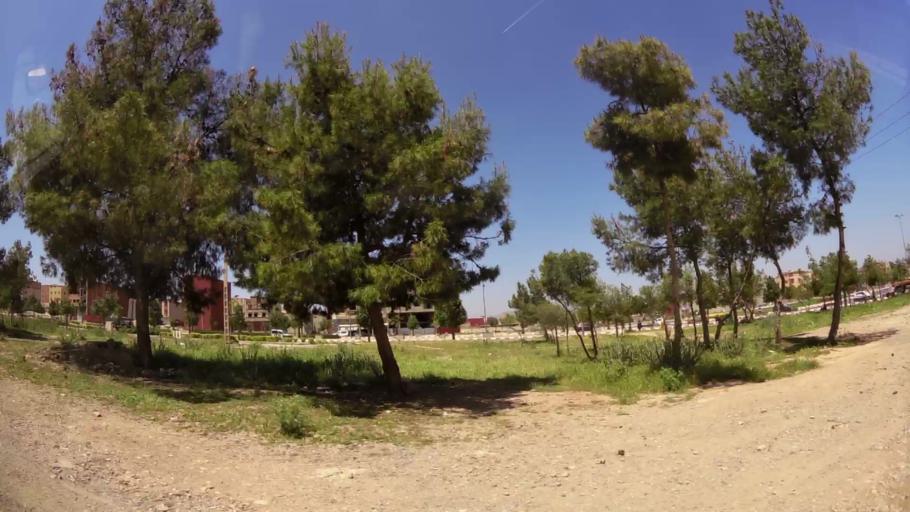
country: MA
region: Oriental
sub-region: Oujda-Angad
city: Oujda
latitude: 34.6820
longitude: -1.9456
